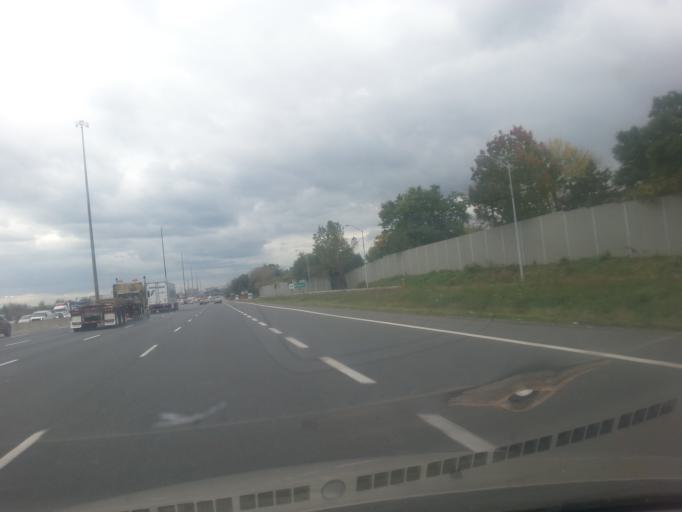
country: CA
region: Ontario
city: Ajax
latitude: 43.8489
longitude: -79.0420
